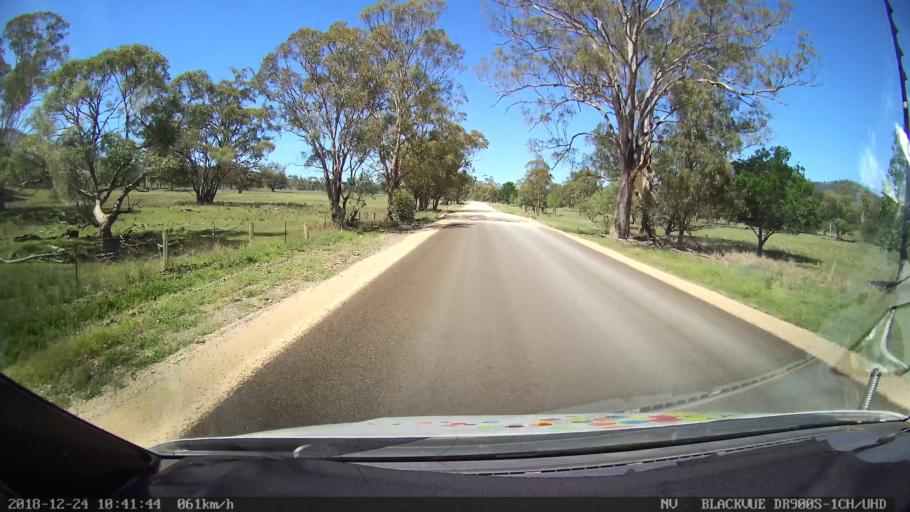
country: AU
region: New South Wales
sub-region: Upper Hunter Shire
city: Merriwa
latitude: -31.8713
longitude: 150.4572
